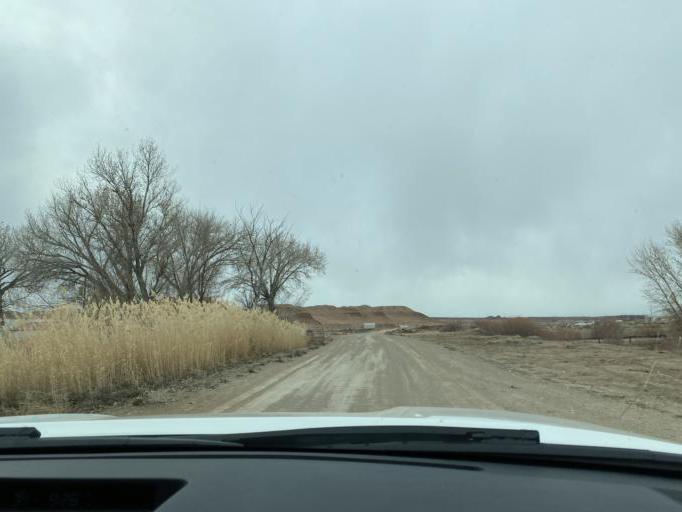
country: US
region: Utah
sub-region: Emery County
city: Ferron
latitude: 38.3694
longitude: -110.7122
